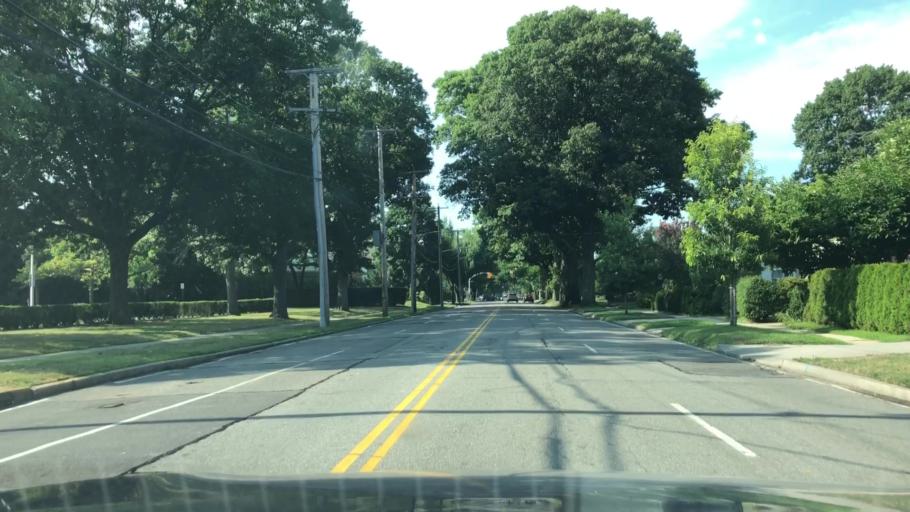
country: US
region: New York
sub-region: Nassau County
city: Stewart Manor
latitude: 40.7233
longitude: -73.6793
